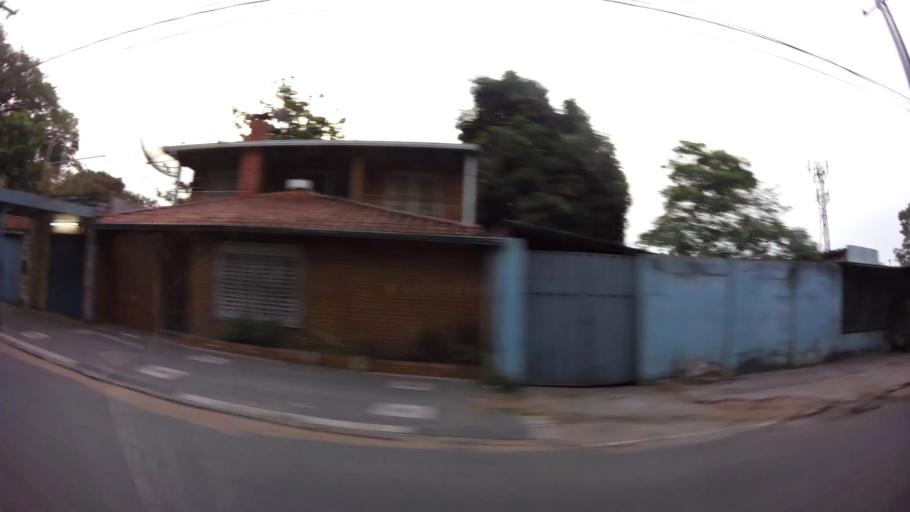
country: PY
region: Central
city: Lambare
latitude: -25.3316
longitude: -57.6199
